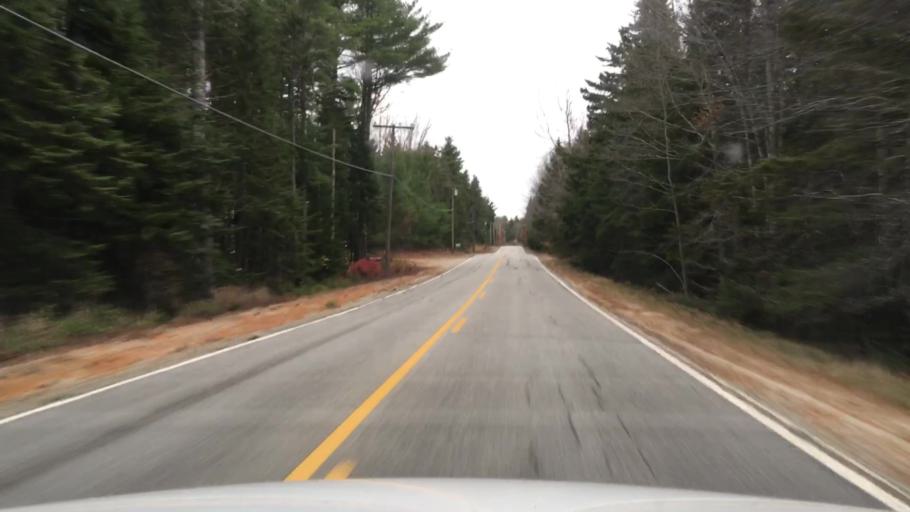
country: US
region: Maine
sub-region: Hancock County
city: Sedgwick
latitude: 44.2836
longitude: -68.5545
